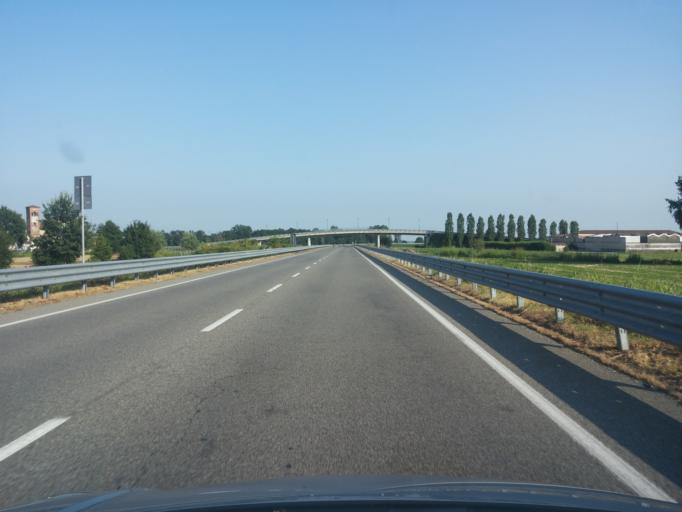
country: IT
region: Piedmont
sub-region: Provincia di Biella
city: Castelletto Cervo
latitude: 45.5203
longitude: 8.2053
